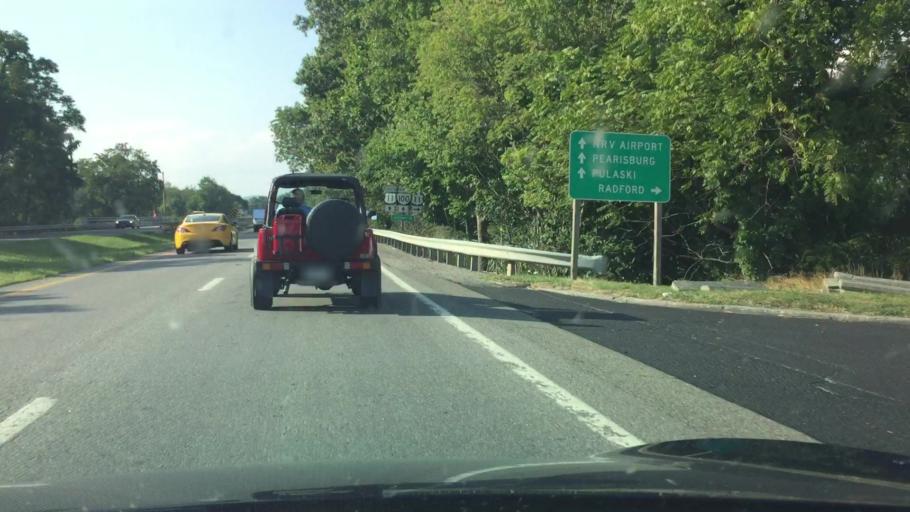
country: US
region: Virginia
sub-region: Pulaski County
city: Dublin
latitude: 37.1004
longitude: -80.6907
